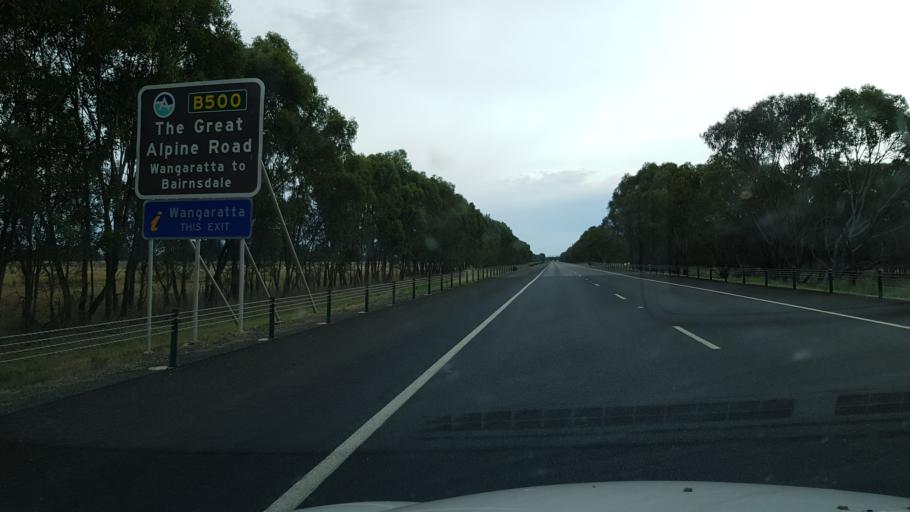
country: AU
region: Victoria
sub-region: Wangaratta
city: Wangaratta
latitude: -36.2934
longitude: 146.3883
